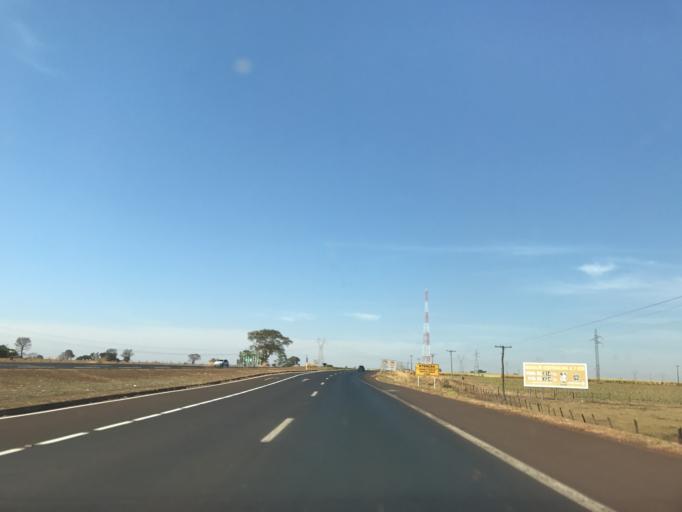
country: BR
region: Goias
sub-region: Itumbiara
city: Itumbiara
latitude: -18.4989
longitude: -49.1890
